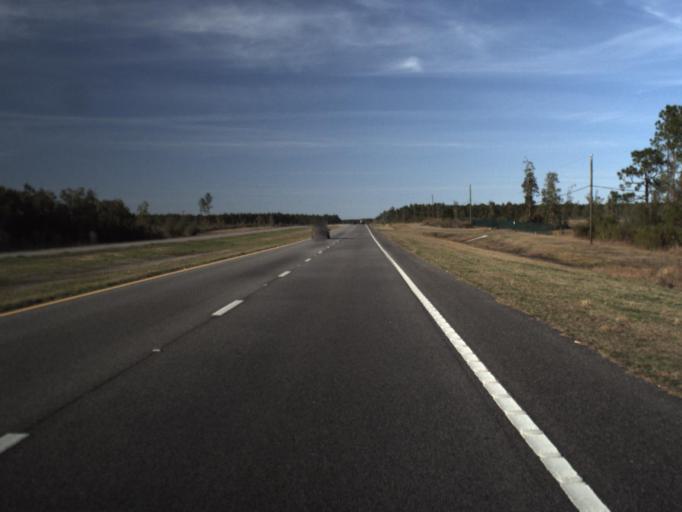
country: US
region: Florida
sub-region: Bay County
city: Laguna Beach
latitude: 30.3430
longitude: -85.8587
